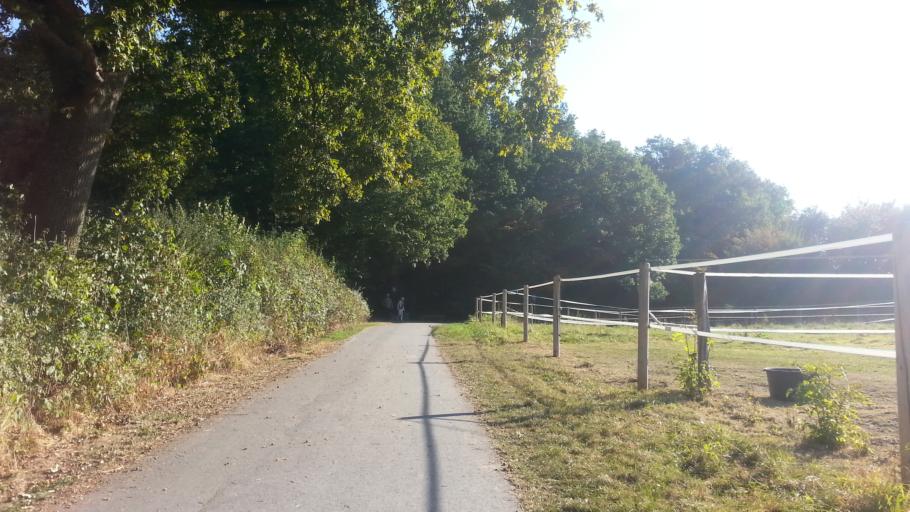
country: DE
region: North Rhine-Westphalia
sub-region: Regierungsbezirk Munster
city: Muenster
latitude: 51.9417
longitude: 7.5872
